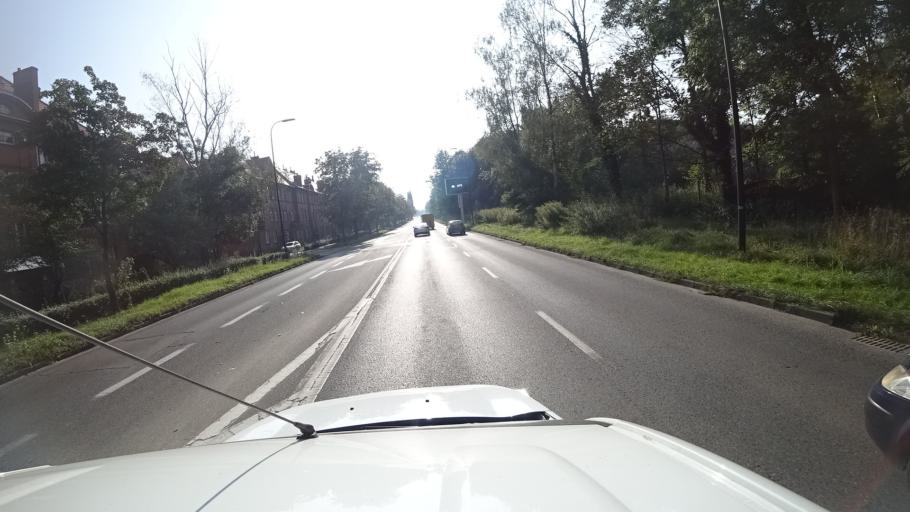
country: PL
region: Silesian Voivodeship
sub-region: Gliwice
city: Gliwice
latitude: 50.2818
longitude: 18.6847
